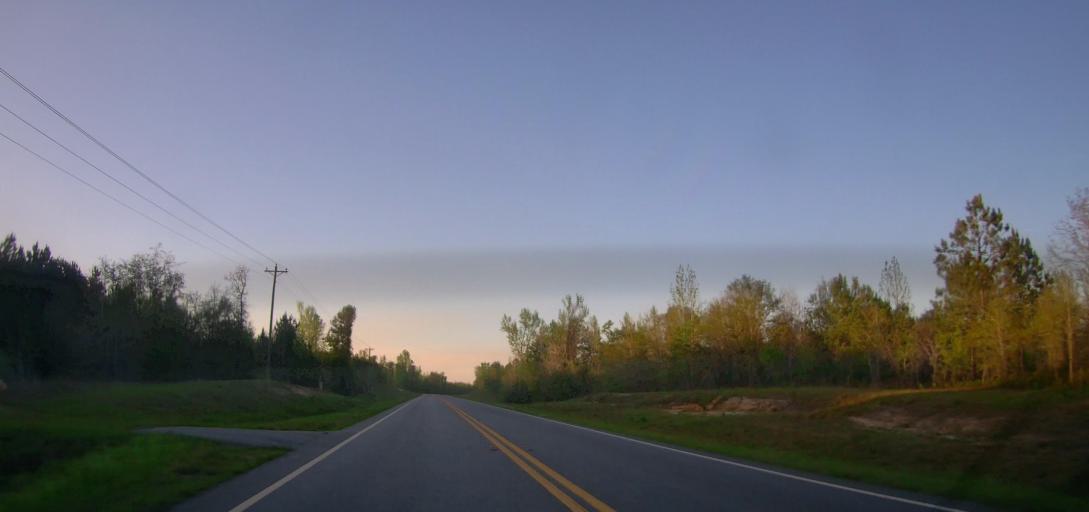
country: US
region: Georgia
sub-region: Talbot County
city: Talbotton
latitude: 32.5547
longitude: -84.5694
